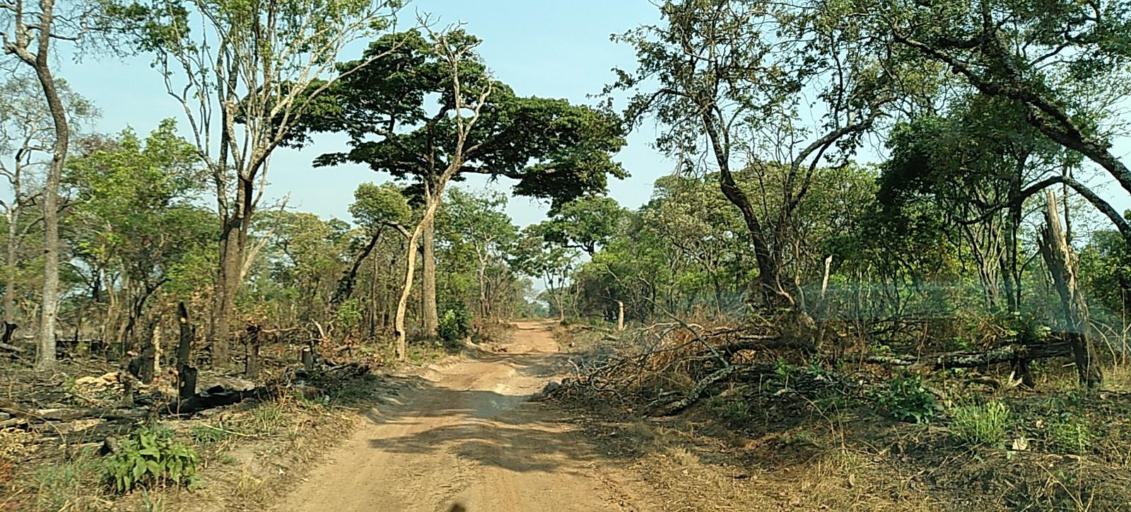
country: ZM
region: North-Western
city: Kansanshi
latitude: -12.2680
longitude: 26.9521
